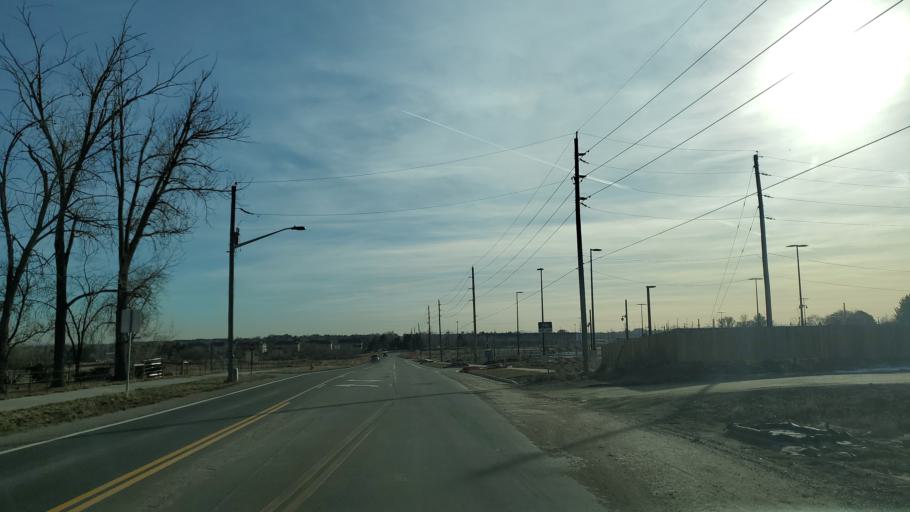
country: US
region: Colorado
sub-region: Adams County
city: Northglenn
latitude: 39.9037
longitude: -104.9589
